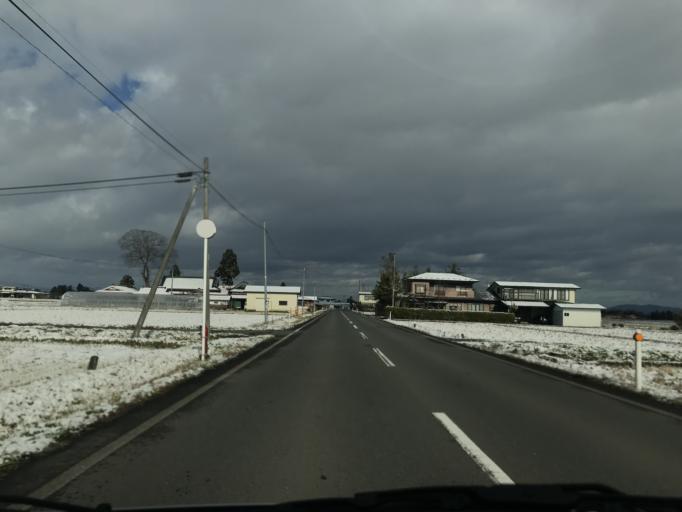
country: JP
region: Iwate
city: Mizusawa
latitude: 39.1478
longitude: 141.1135
